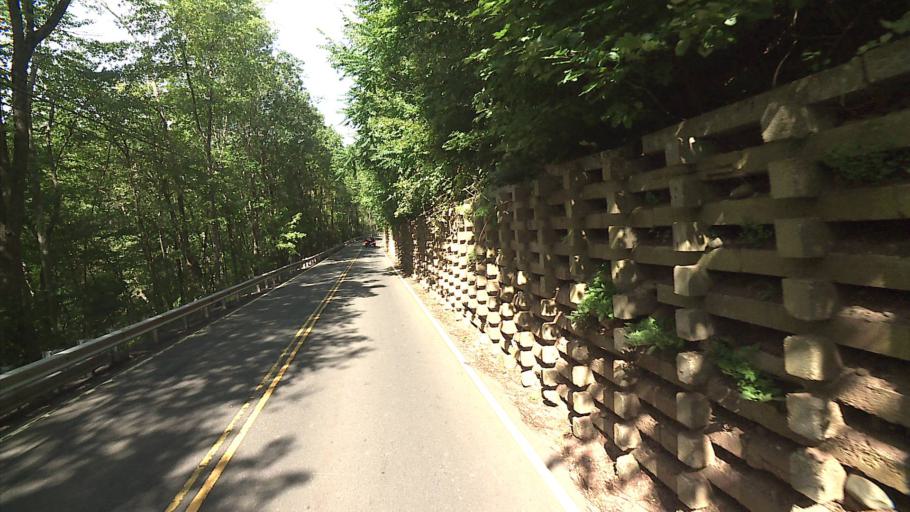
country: US
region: Connecticut
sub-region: New Haven County
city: Meriden
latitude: 41.5288
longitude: -72.8554
